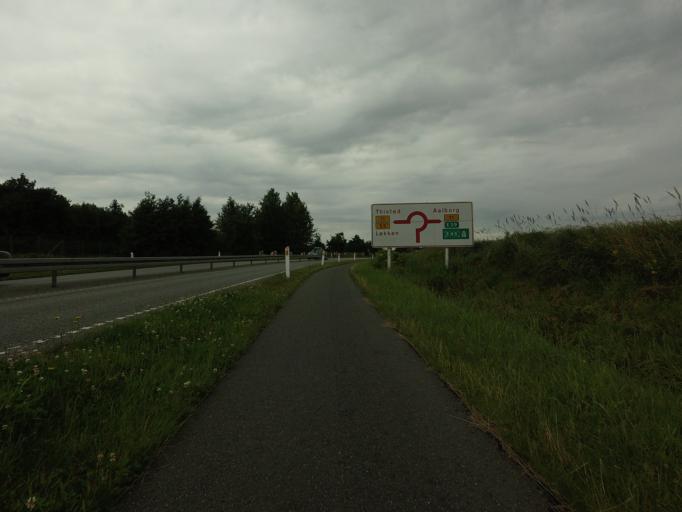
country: DK
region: North Denmark
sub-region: Alborg Kommune
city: Vadum
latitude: 57.1006
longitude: 9.8850
